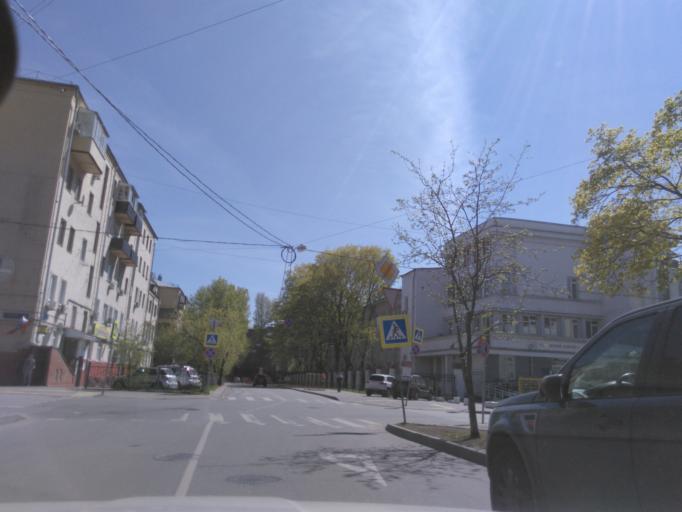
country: RU
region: Moscow
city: Luzhniki
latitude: 55.7228
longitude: 37.5662
